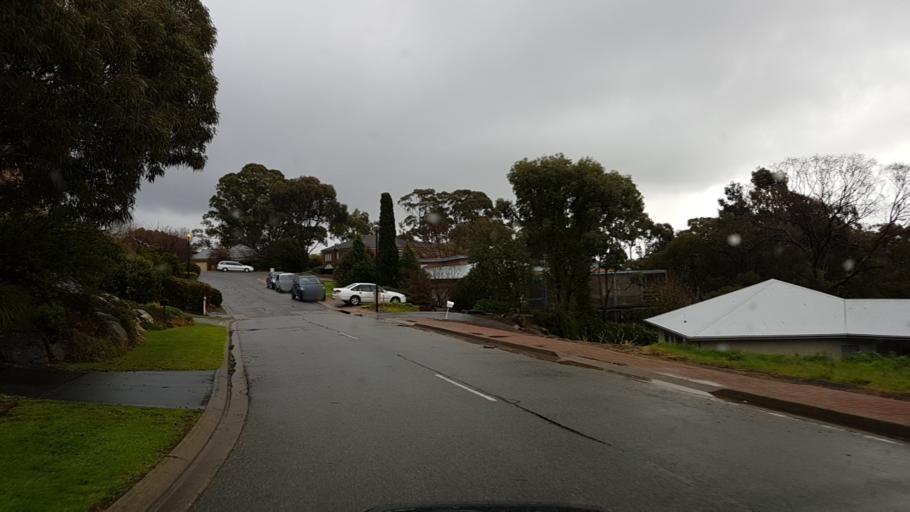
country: AU
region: South Australia
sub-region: Onkaparinga
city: Craigburn Farm
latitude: -35.0862
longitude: 138.5976
